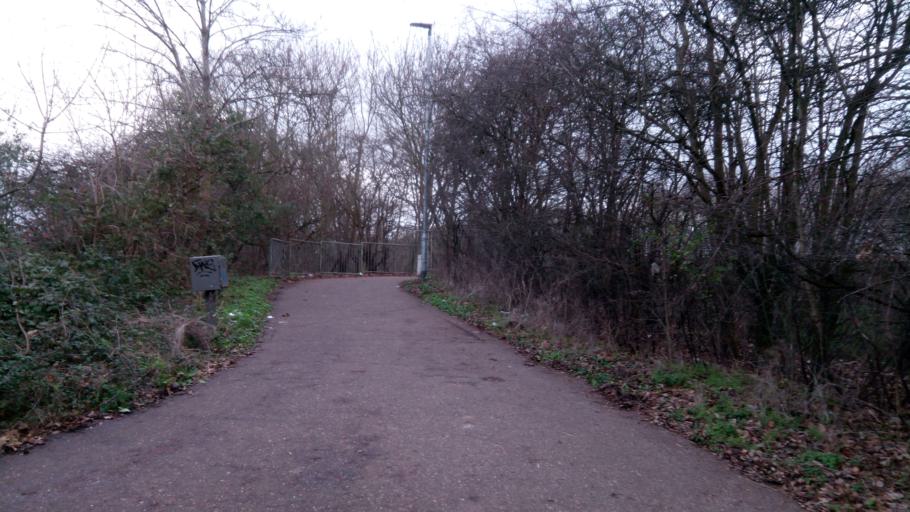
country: GB
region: England
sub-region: Peterborough
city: Marholm
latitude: 52.5771
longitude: -0.2850
